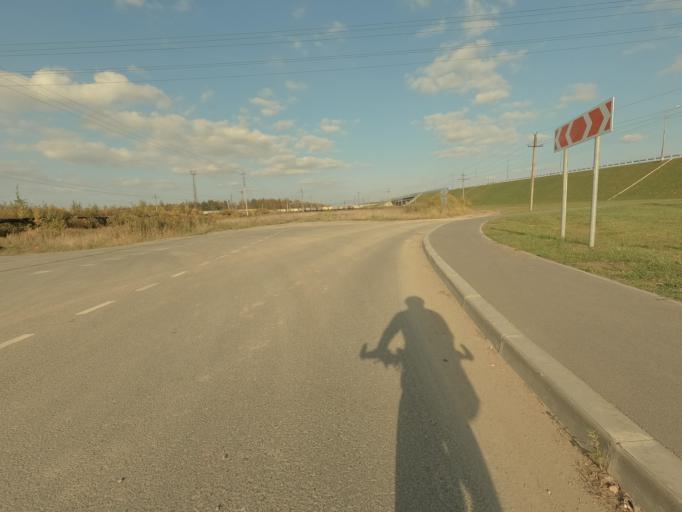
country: RU
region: Leningrad
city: Mga
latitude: 59.7519
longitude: 31.0891
